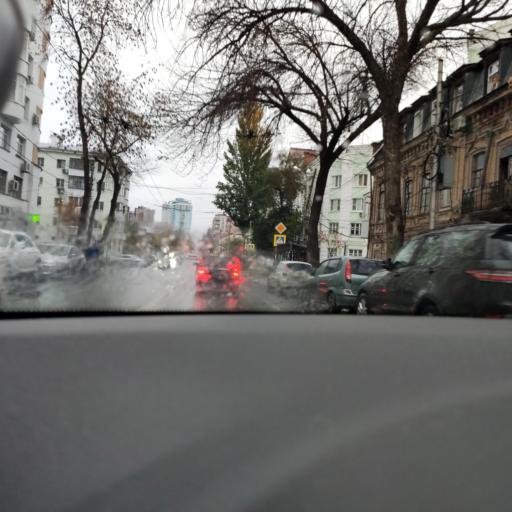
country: RU
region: Samara
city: Samara
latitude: 53.1981
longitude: 50.1126
